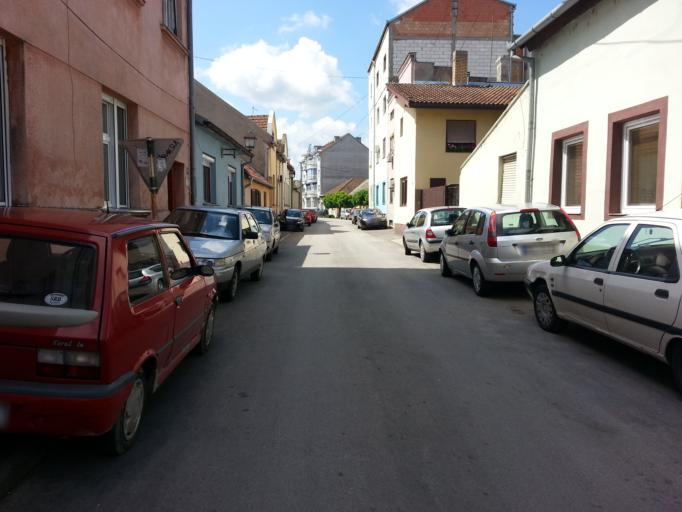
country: RS
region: Autonomna Pokrajina Vojvodina
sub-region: Juznobacki Okrug
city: Novi Sad
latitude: 45.2630
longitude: 19.8453
